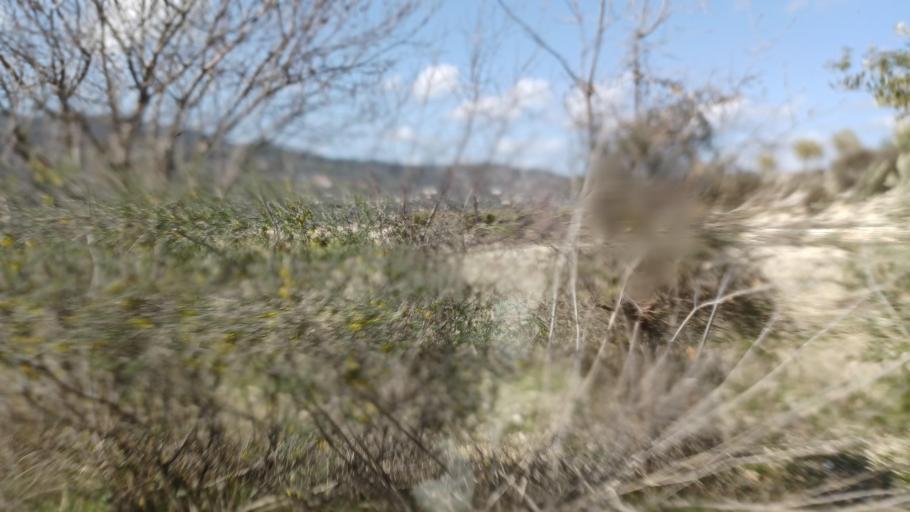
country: CY
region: Limassol
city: Pachna
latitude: 34.8449
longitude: 32.7331
